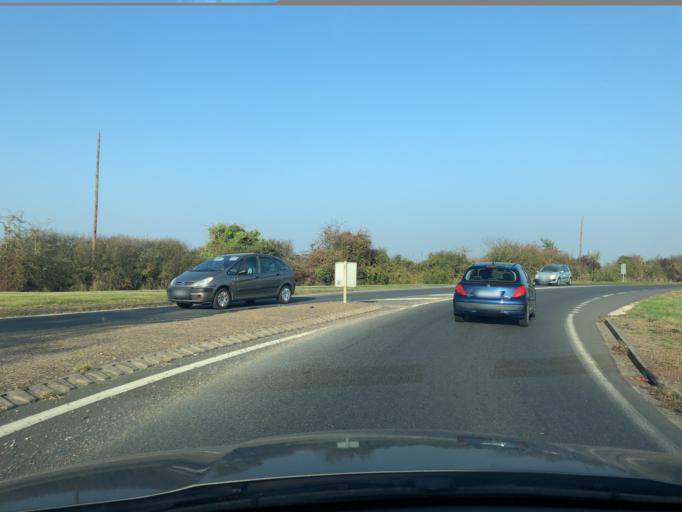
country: FR
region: Centre
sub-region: Departement d'Indre-et-Loire
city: Chanceaux-sur-Choisille
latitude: 47.4498
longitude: 0.6979
